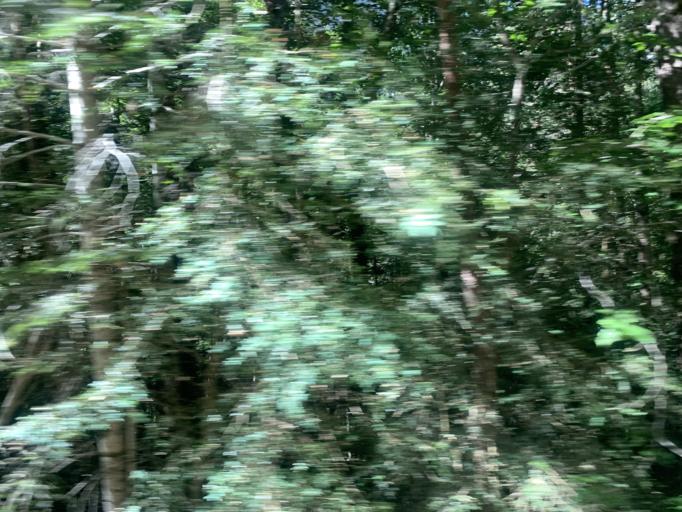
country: ES
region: Aragon
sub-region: Provincia de Huesca
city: Broto
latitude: 42.6525
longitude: -0.0751
